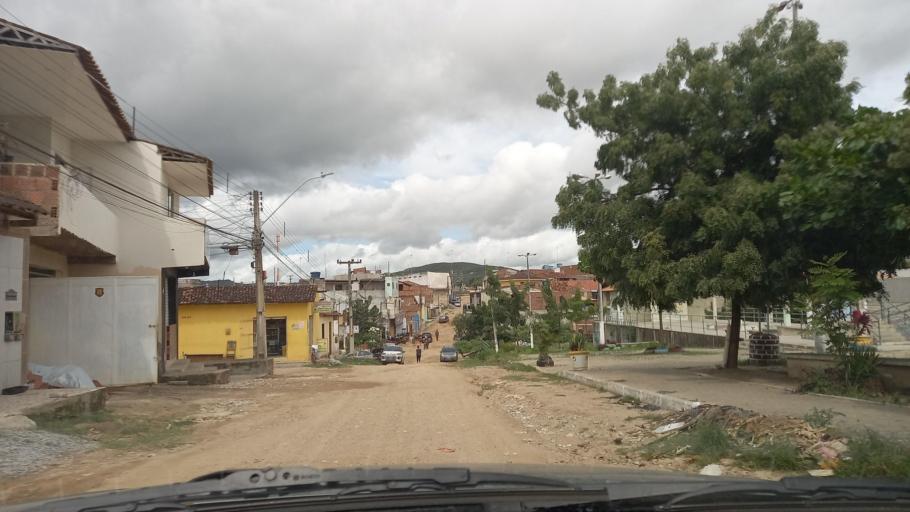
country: ET
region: Oromiya
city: Gore
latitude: 8.1949
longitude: 35.5779
